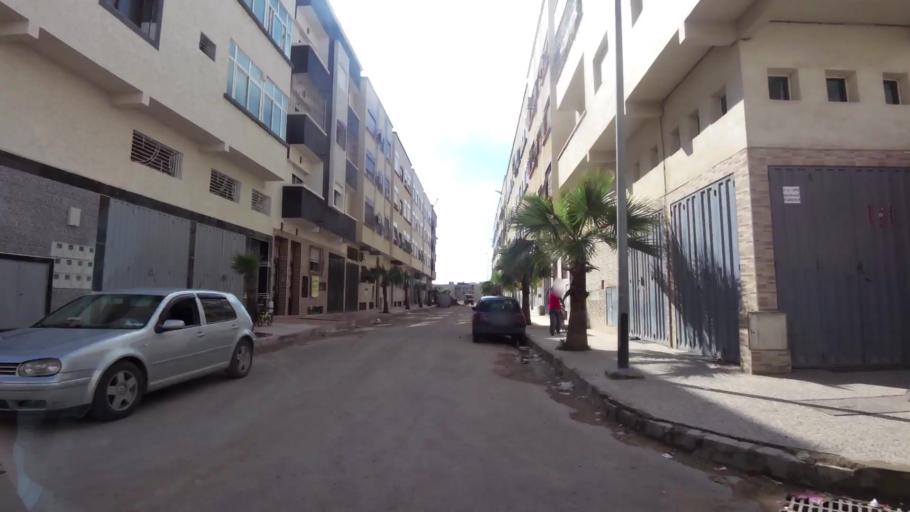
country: MA
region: Chaouia-Ouardigha
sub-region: Settat Province
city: Berrechid
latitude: 33.2594
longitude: -7.5637
